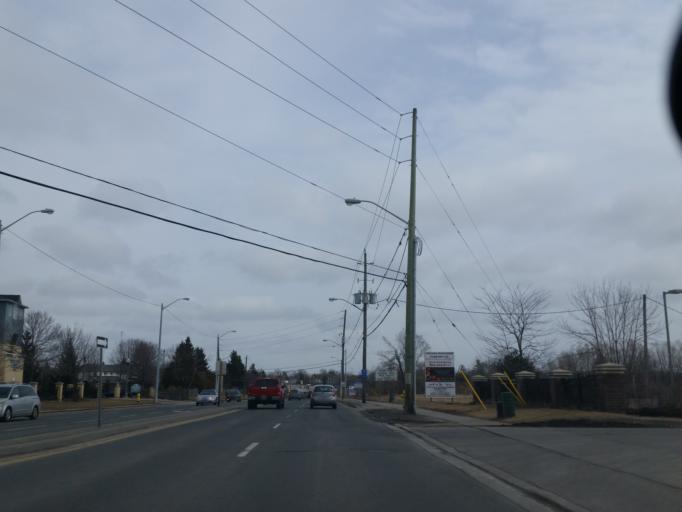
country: CA
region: Ontario
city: Oshawa
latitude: 43.9070
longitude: -78.8076
